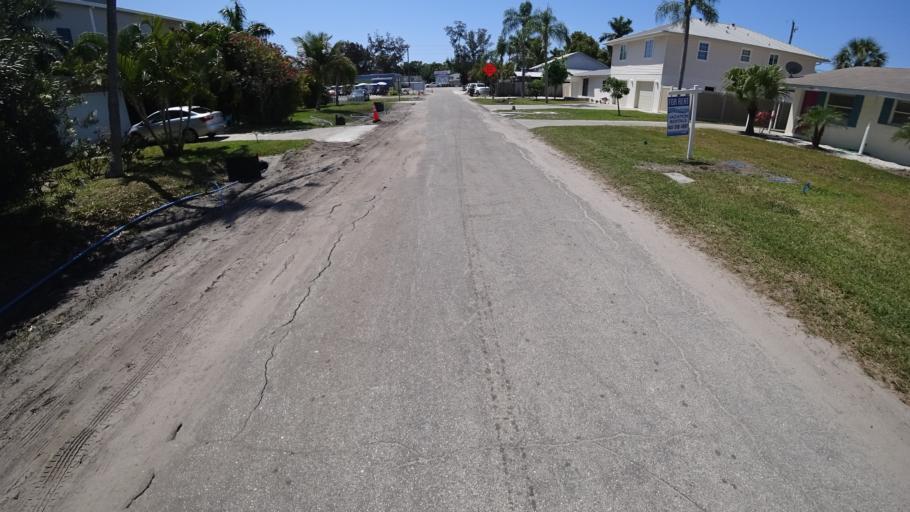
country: US
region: Florida
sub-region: Manatee County
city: Cortez
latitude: 27.4701
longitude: -82.6848
